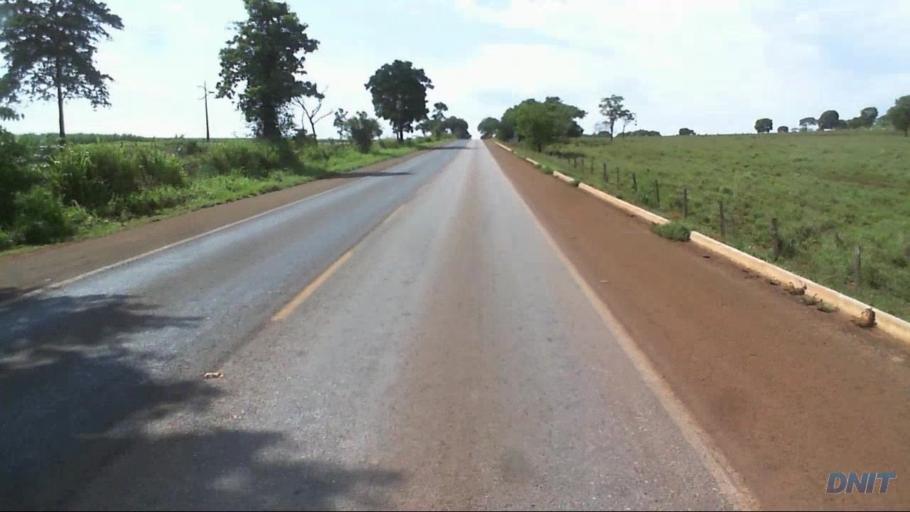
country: BR
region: Goias
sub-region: Barro Alto
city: Barro Alto
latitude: -15.0158
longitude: -48.8992
